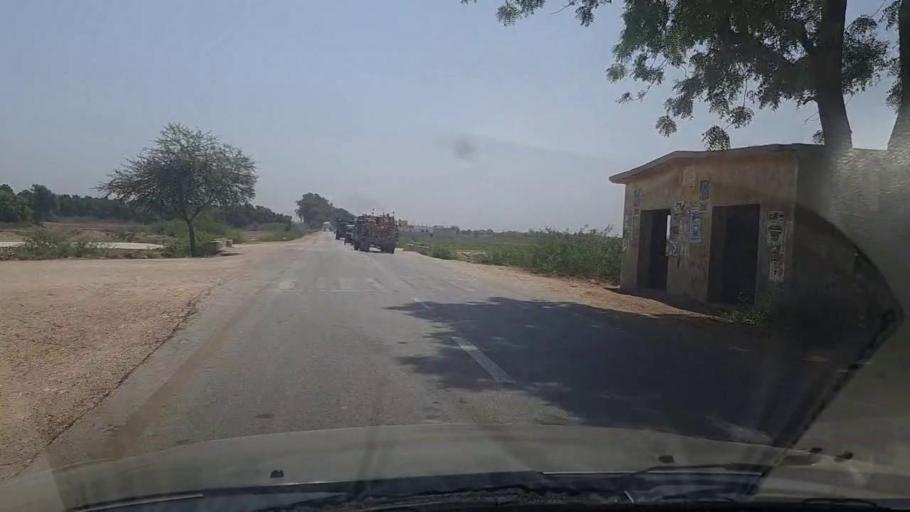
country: PK
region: Sindh
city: Tando Jam
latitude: 25.3674
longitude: 68.4804
